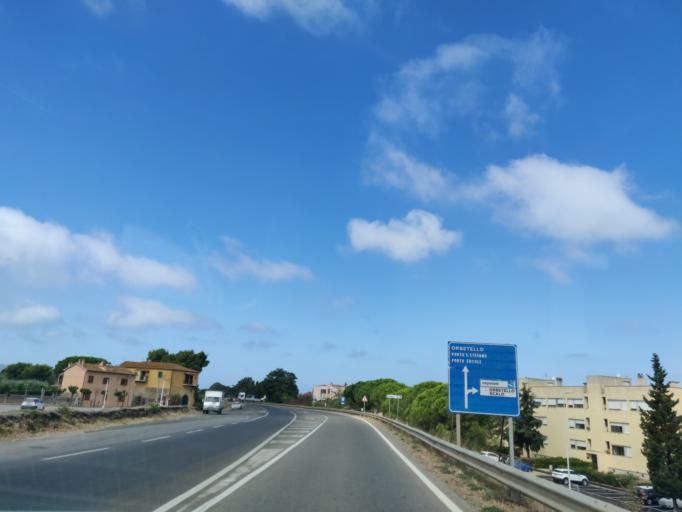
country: IT
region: Tuscany
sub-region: Provincia di Grosseto
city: Orbetello Scalo
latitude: 42.4466
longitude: 11.2518
